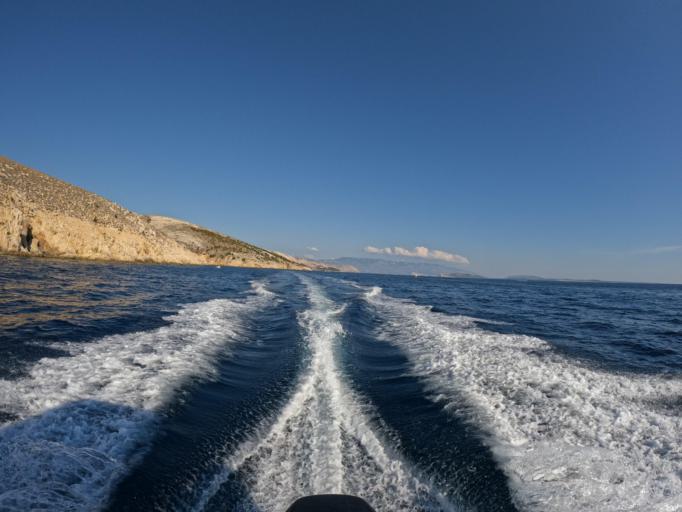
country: HR
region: Primorsko-Goranska
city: Punat
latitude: 44.9680
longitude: 14.6424
